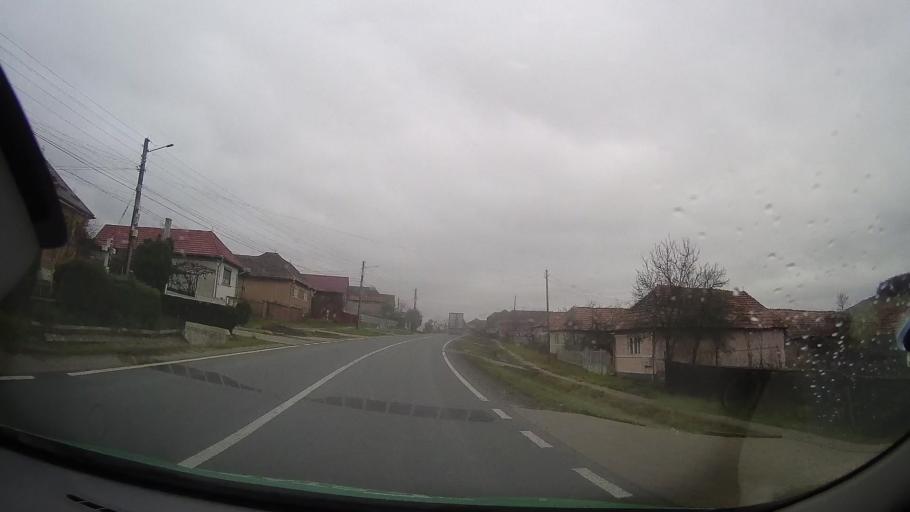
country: RO
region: Mures
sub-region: Comuna Lunca
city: Lunca
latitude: 46.8556
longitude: 24.5693
